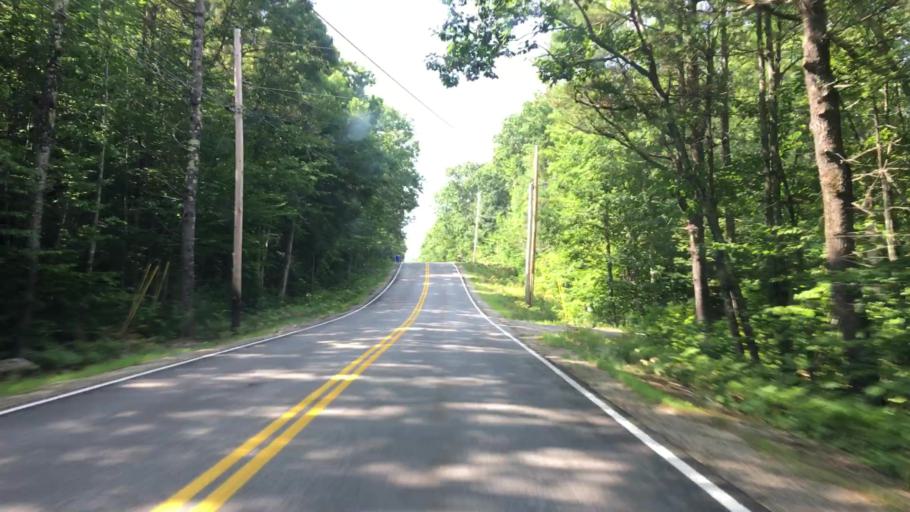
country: US
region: Maine
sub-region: Cumberland County
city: Raymond
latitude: 43.9671
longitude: -70.4121
